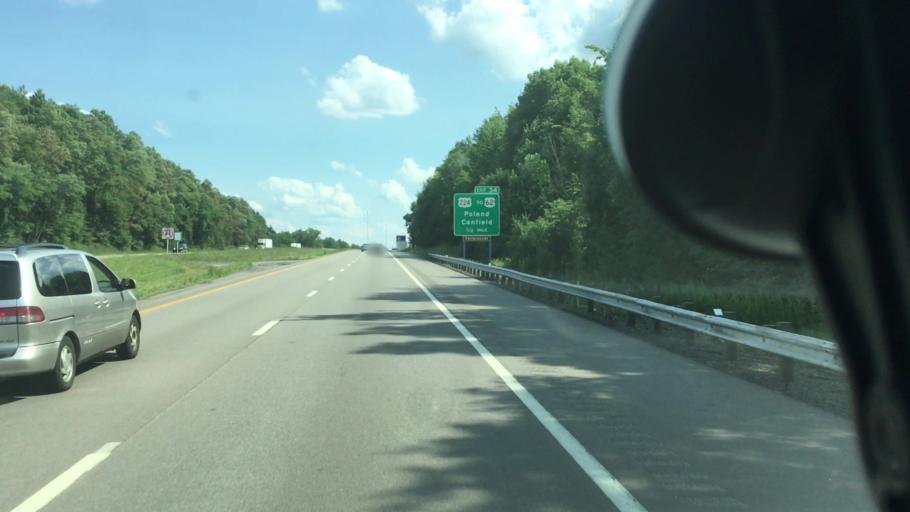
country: US
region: Ohio
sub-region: Mahoning County
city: Canfield
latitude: 41.0370
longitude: -80.7421
